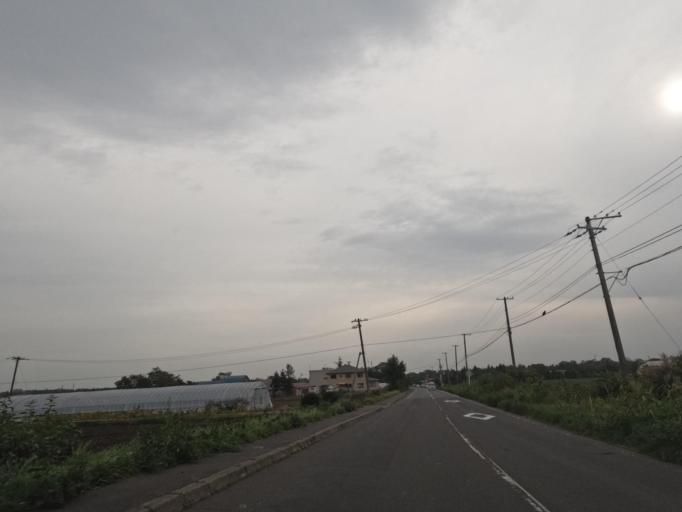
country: JP
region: Hokkaido
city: Date
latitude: 42.4996
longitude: 140.8755
